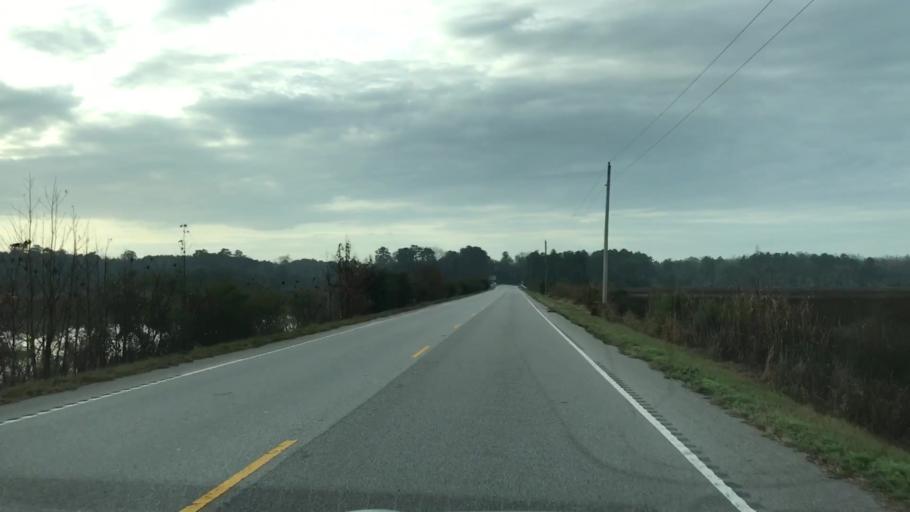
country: US
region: South Carolina
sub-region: Jasper County
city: Ridgeland
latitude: 32.5468
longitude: -80.9127
